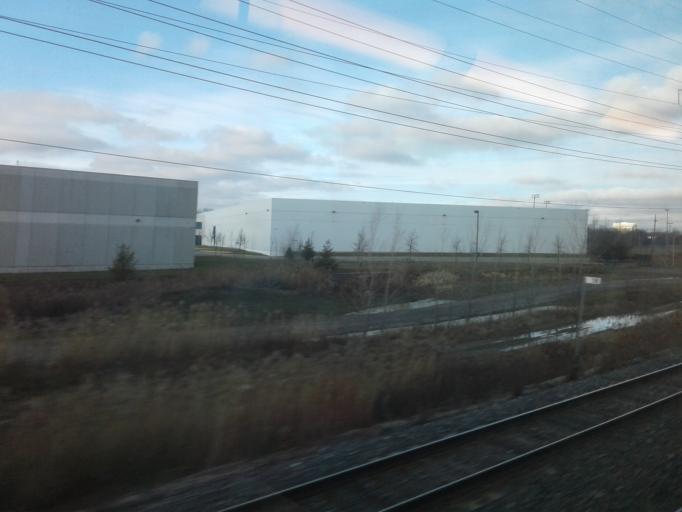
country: CA
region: Ontario
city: Oakville
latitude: 43.4966
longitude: -79.6487
